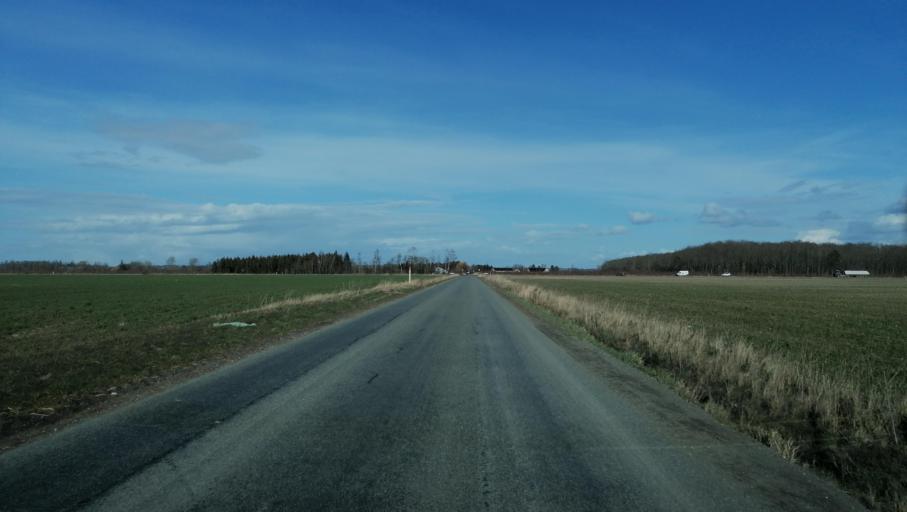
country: DK
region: Zealand
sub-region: Odsherred Kommune
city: Horve
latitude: 55.7607
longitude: 11.5009
